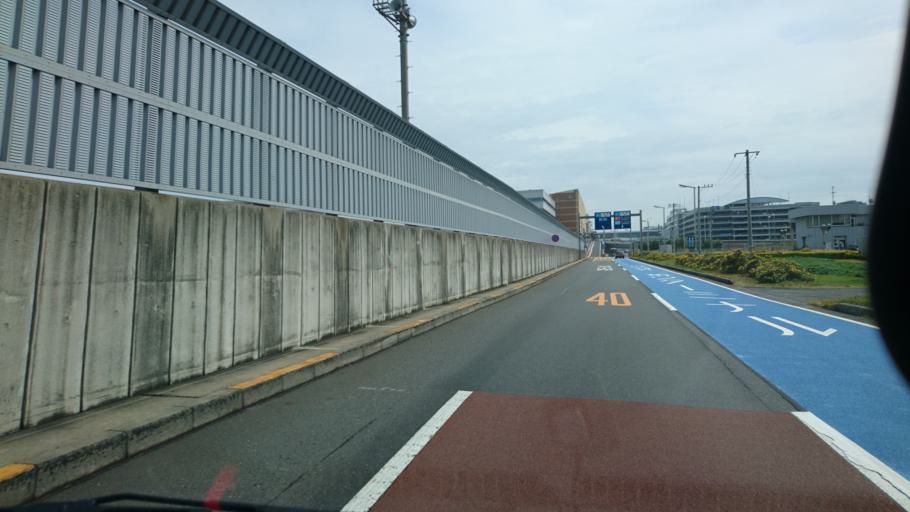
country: JP
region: Kanagawa
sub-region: Kawasaki-shi
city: Kawasaki
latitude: 35.5556
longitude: 139.7849
